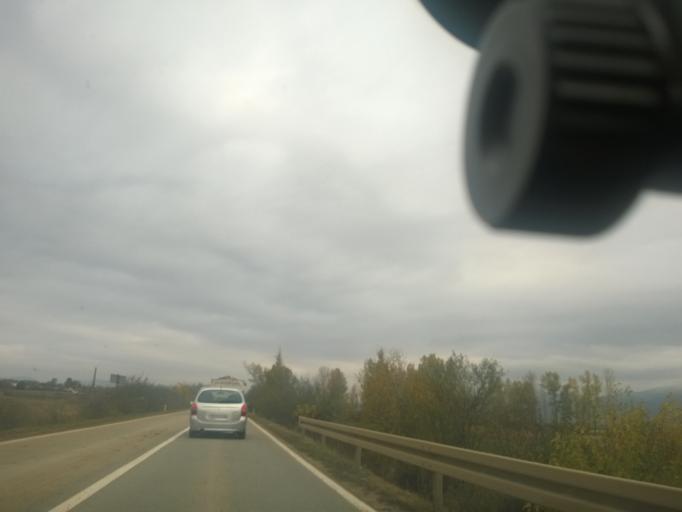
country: RS
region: Central Serbia
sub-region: Pirotski Okrug
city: Dimitrovgrad
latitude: 43.0662
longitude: 22.6776
